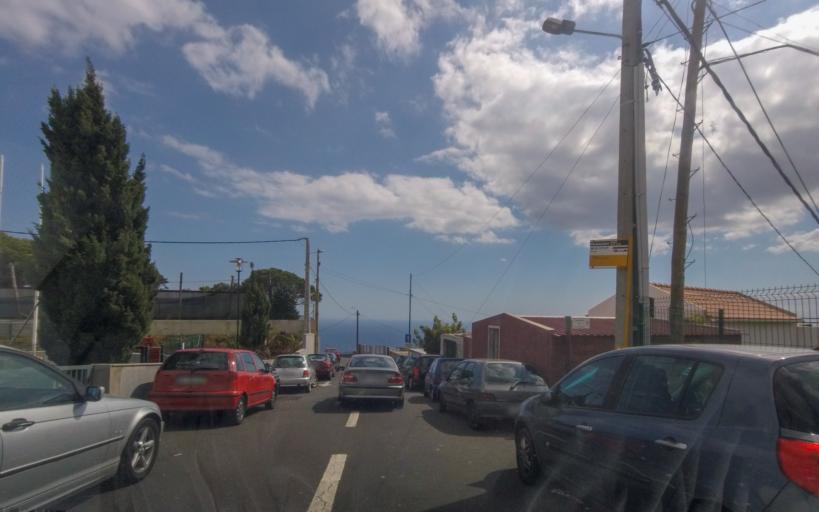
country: PT
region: Madeira
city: Camara de Lobos
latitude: 32.6529
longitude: -16.9500
